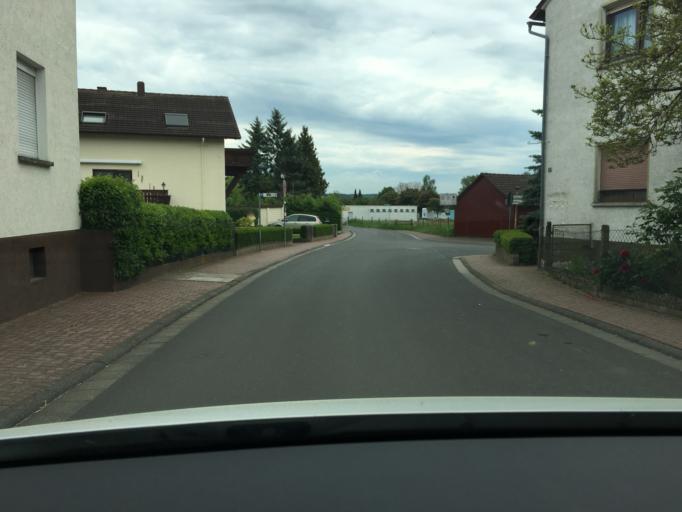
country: DE
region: Hesse
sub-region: Regierungsbezirk Giessen
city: Hungen
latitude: 50.4564
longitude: 8.8988
